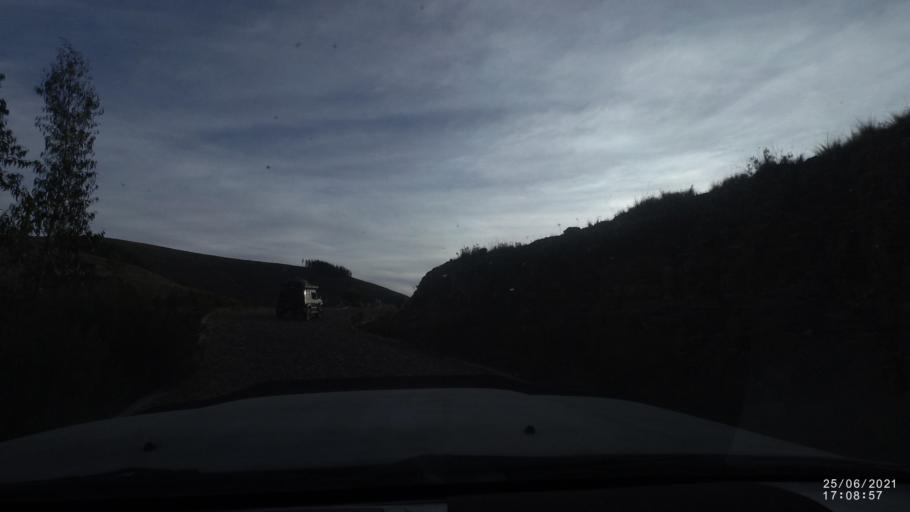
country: BO
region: Cochabamba
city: Arani
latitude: -17.8383
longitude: -65.7072
